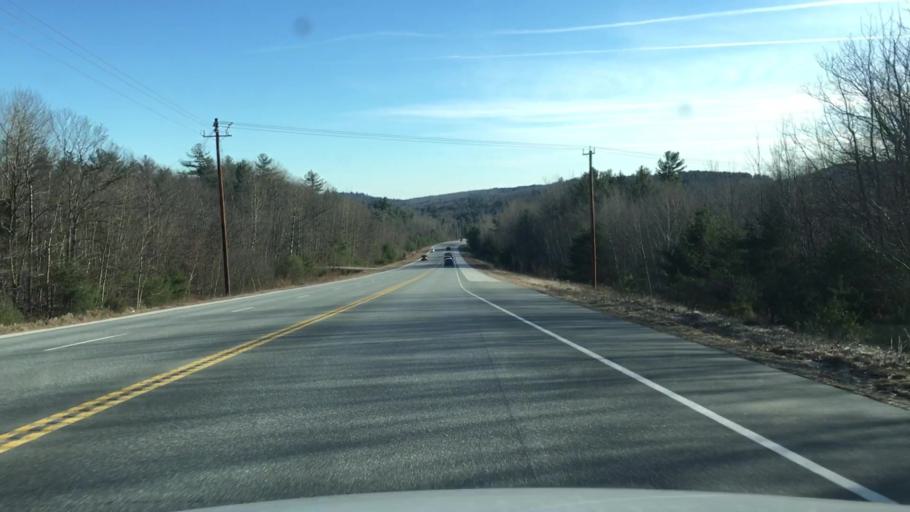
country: US
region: Maine
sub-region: Hancock County
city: Dedham
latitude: 44.6870
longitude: -68.5830
